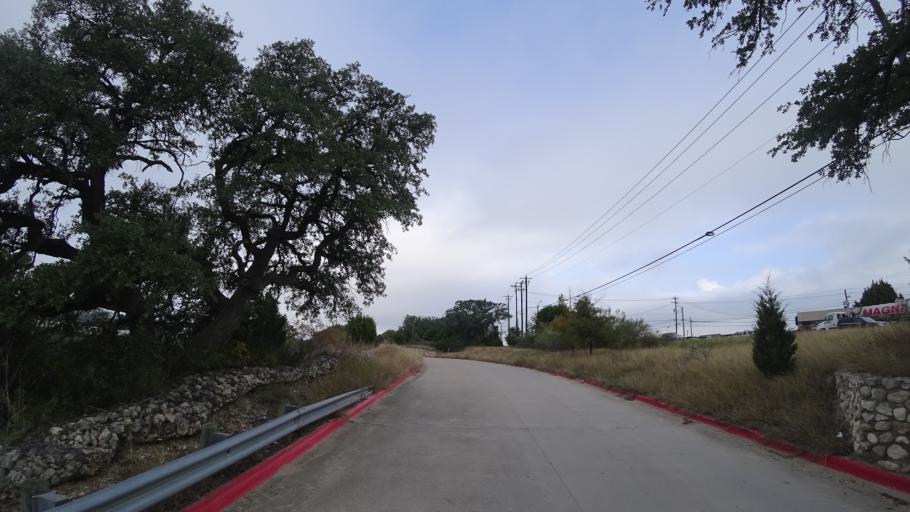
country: US
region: Texas
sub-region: Travis County
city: Bee Cave
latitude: 30.3042
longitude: -97.9352
